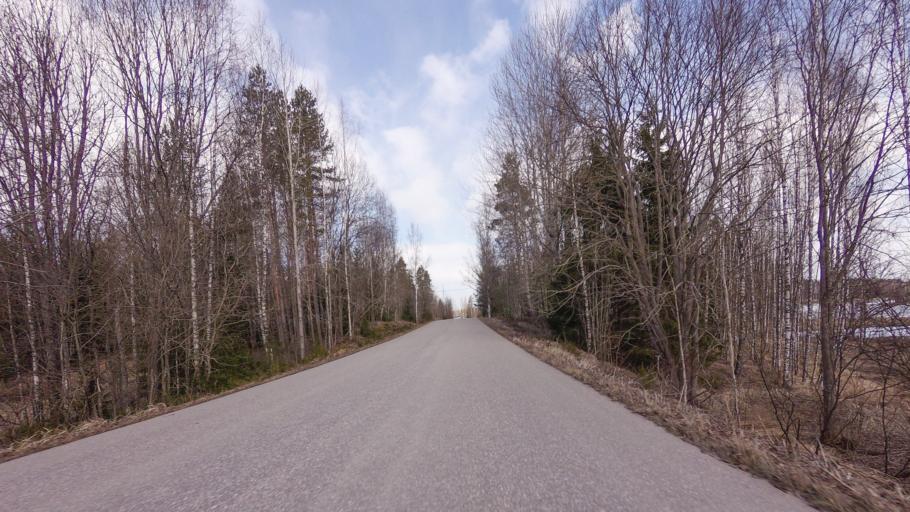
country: FI
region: Varsinais-Suomi
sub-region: Salo
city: Suomusjaervi
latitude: 60.2940
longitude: 23.6405
